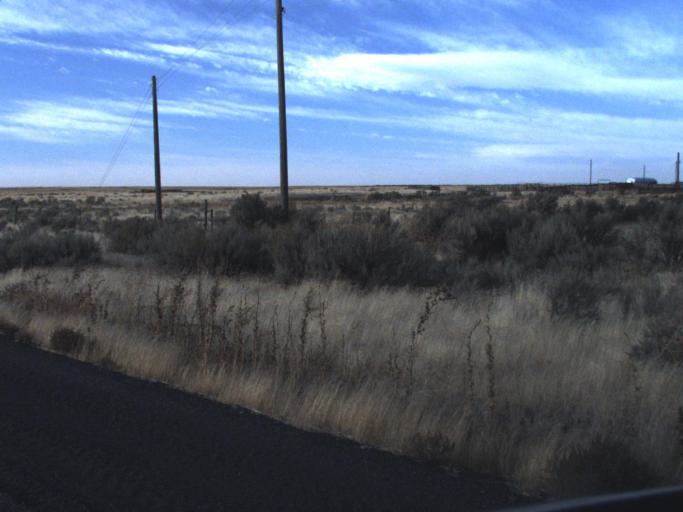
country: US
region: Washington
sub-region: Grant County
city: Warden
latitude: 47.3417
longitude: -118.9110
